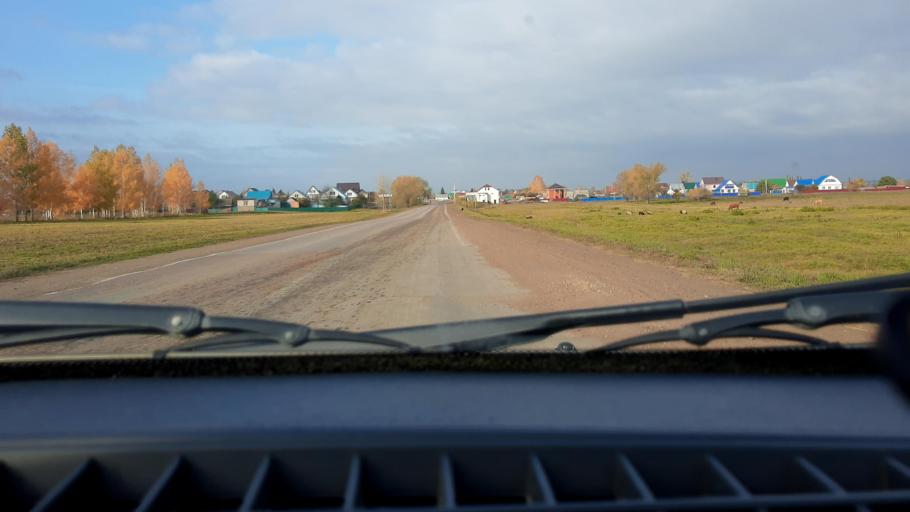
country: RU
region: Bashkortostan
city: Kabakovo
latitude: 54.5481
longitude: 56.1035
